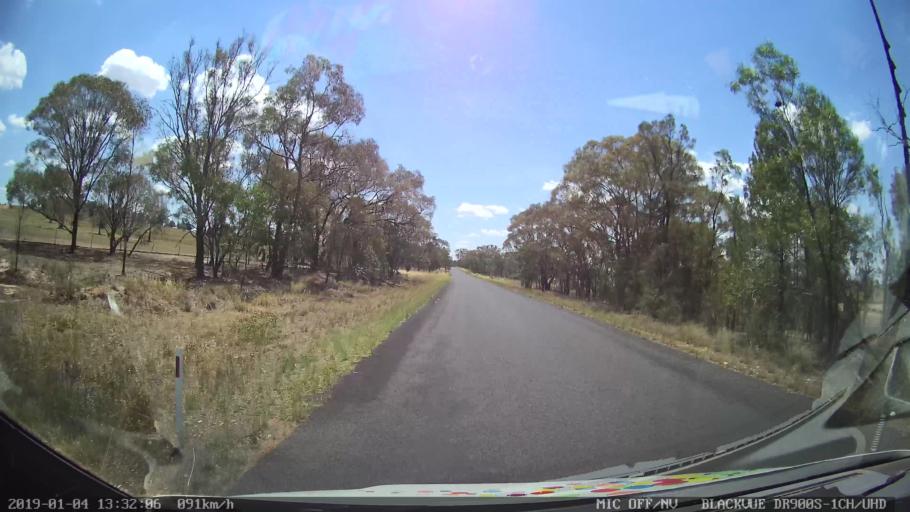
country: AU
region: New South Wales
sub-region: Dubbo Municipality
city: Eulomogo
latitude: -32.6140
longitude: 148.5489
